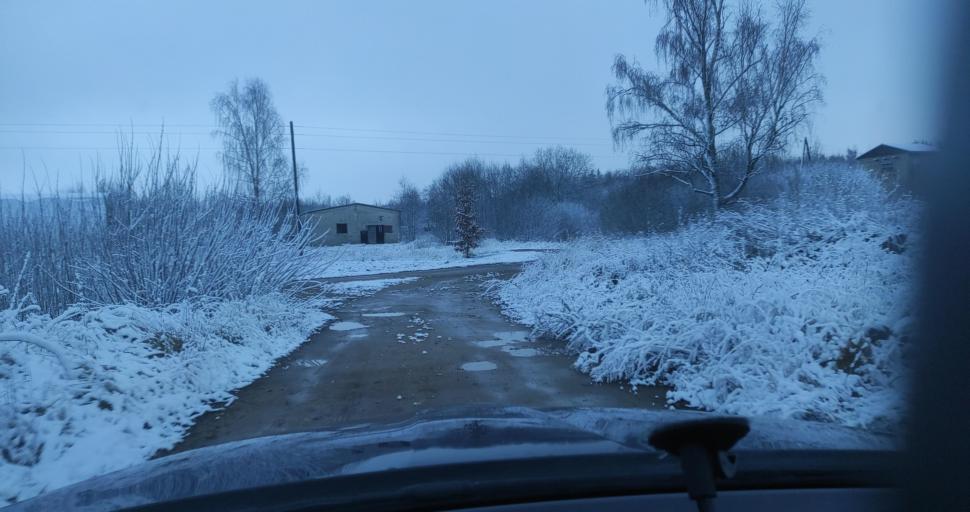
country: LV
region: Skrunda
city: Skrunda
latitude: 56.8694
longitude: 22.2403
